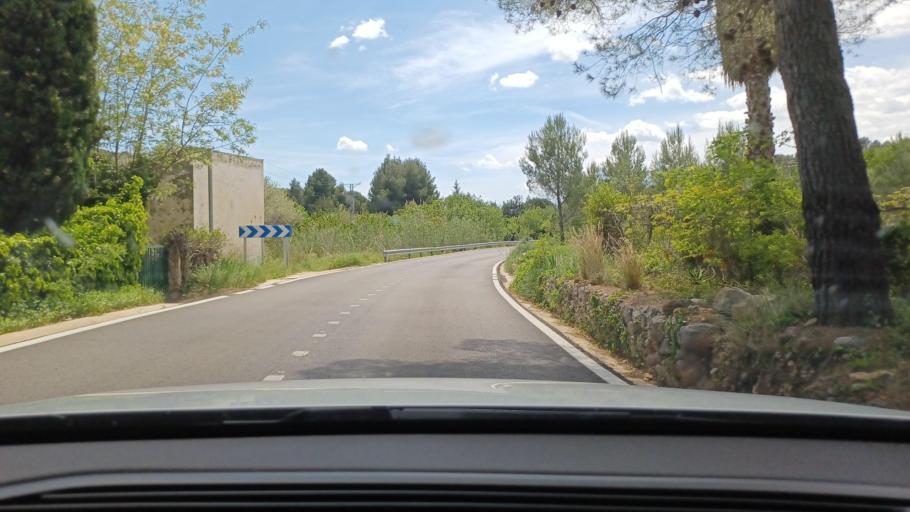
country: ES
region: Valencia
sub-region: Provincia de Castello
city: Rosell
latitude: 40.6547
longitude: 0.2680
